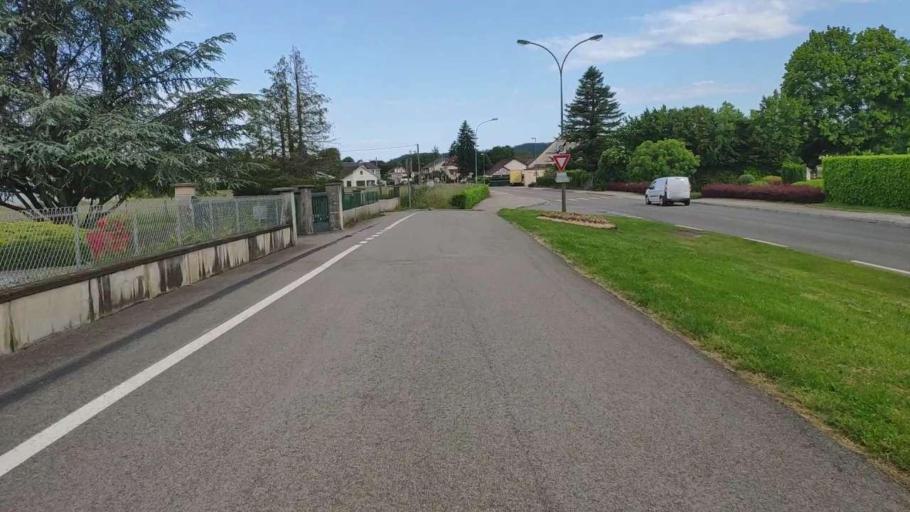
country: FR
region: Franche-Comte
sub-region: Departement du Jura
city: Perrigny
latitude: 46.7617
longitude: 5.6016
